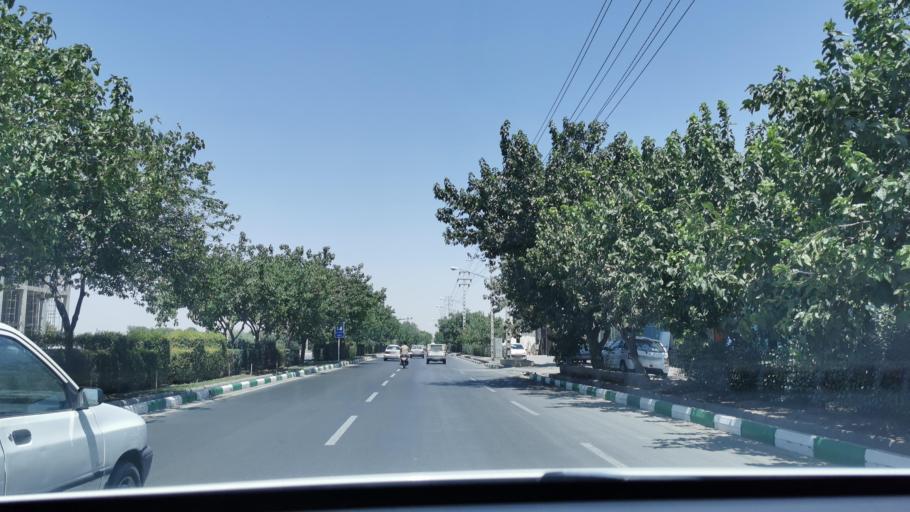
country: IR
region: Razavi Khorasan
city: Mashhad
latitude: 36.3526
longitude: 59.6306
